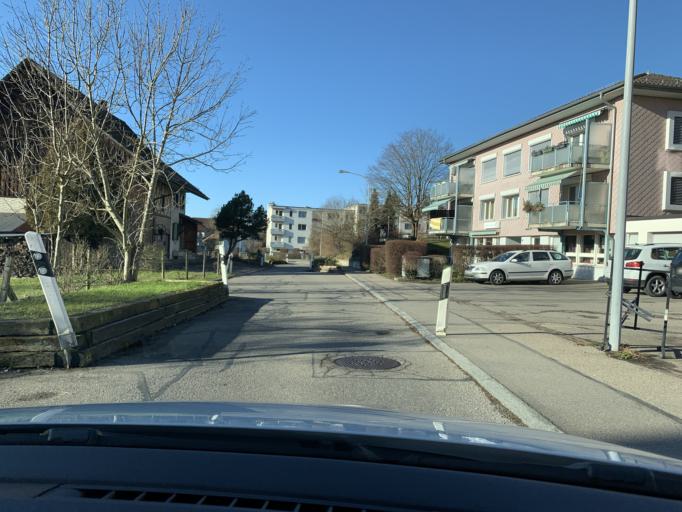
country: CH
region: Zurich
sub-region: Bezirk Dielsdorf
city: Sonnhalde
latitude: 47.4593
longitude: 8.4441
